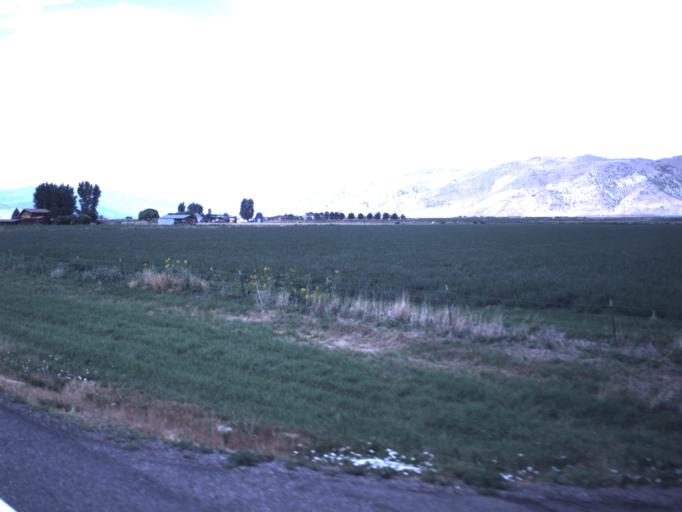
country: US
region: Utah
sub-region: Sevier County
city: Richfield
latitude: 38.7150
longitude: -112.1046
